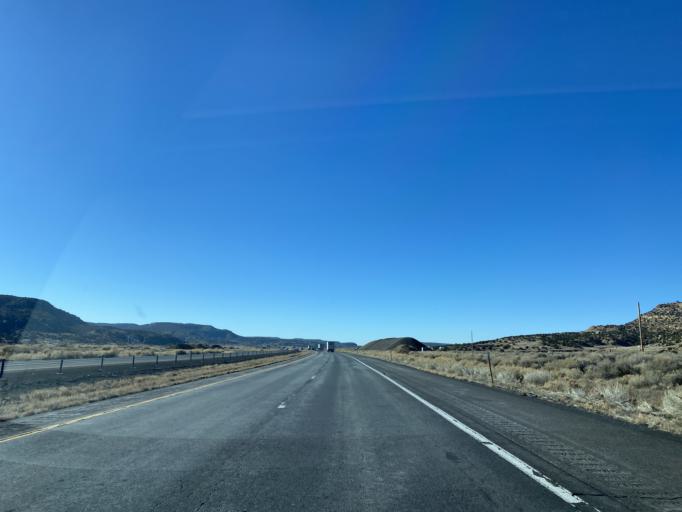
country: US
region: New Mexico
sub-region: McKinley County
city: Gallup
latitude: 35.4567
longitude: -108.9474
